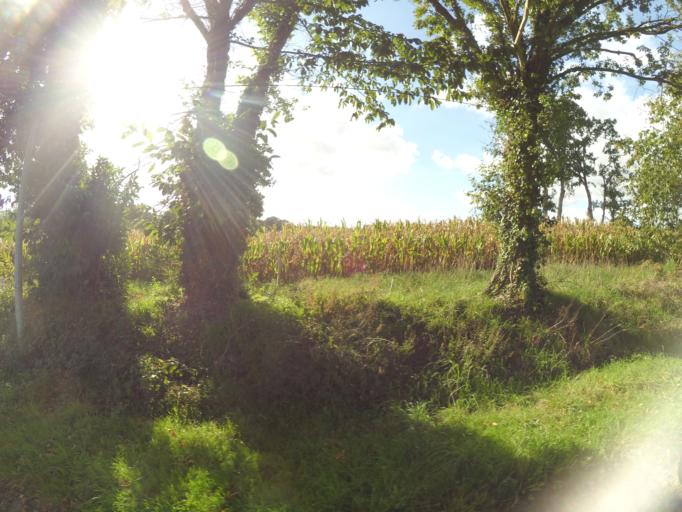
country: FR
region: Brittany
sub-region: Departement du Morbihan
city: Saint-Martin-sur-Oust
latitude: 47.7293
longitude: -2.2521
